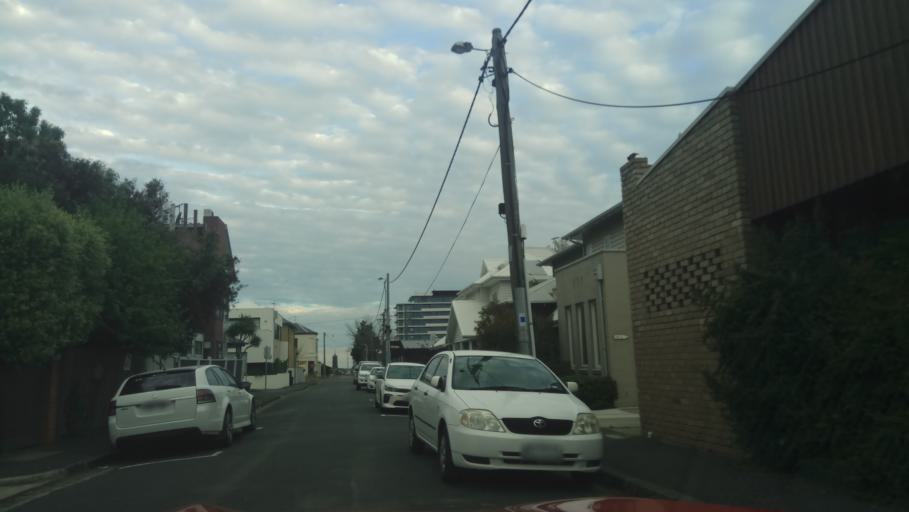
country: AU
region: Victoria
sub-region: Hobsons Bay
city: Williamstown
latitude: -37.8648
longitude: 144.9061
